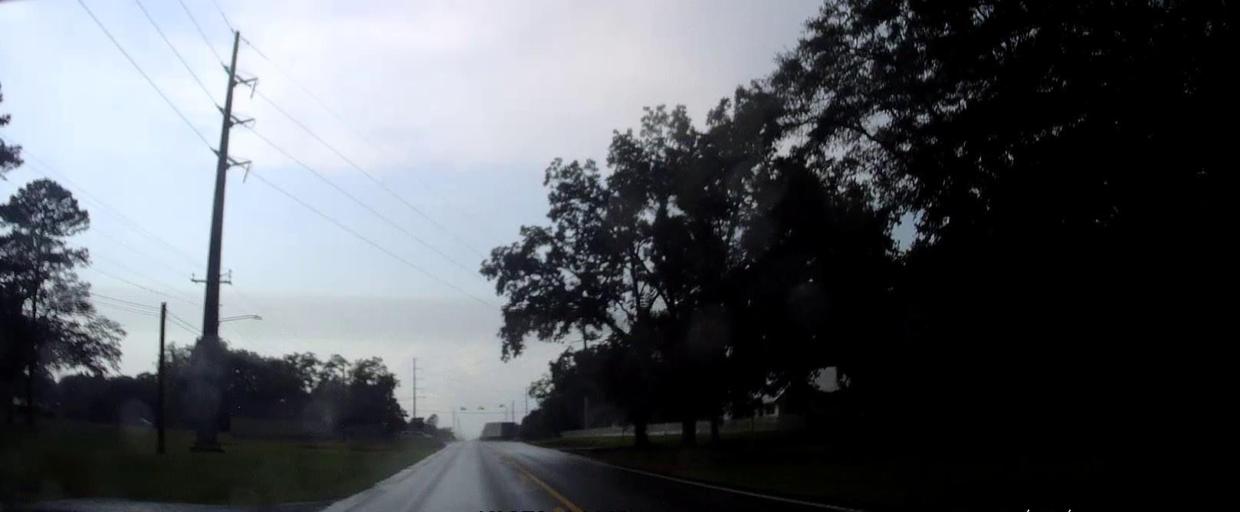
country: US
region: Georgia
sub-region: Twiggs County
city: Jeffersonville
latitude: 32.5898
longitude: -83.2266
